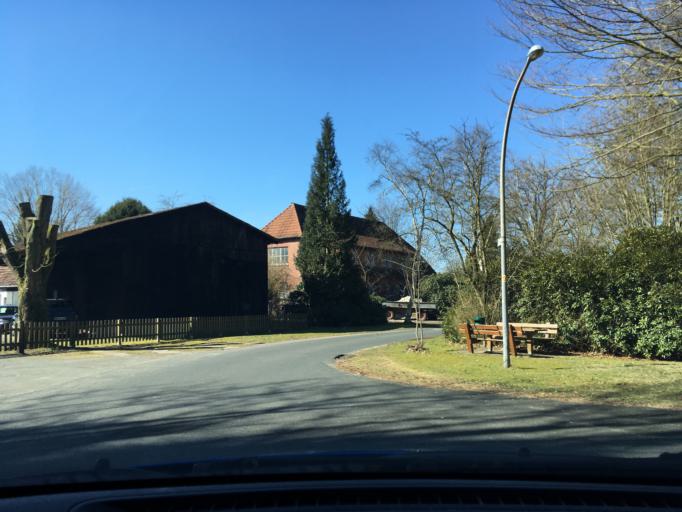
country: DE
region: Lower Saxony
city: Hemslingen
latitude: 53.0823
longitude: 9.6016
